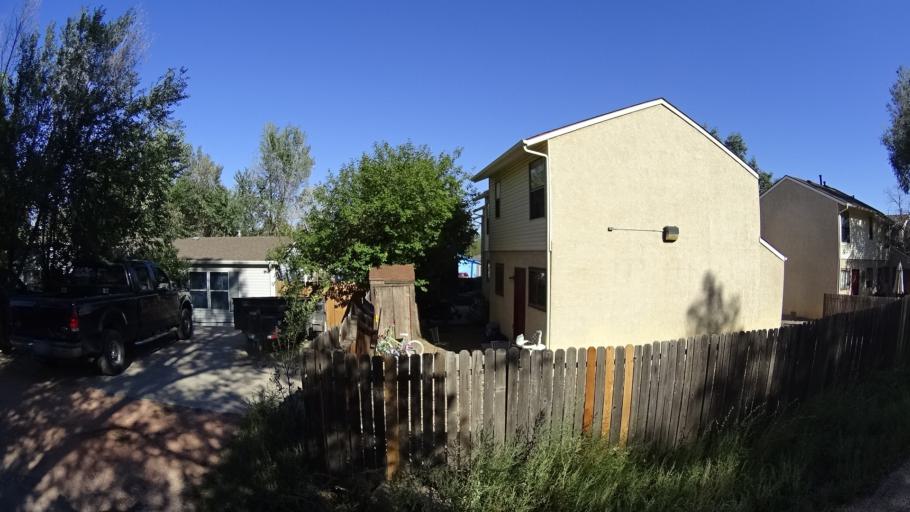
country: US
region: Colorado
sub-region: El Paso County
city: Colorado Springs
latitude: 38.8380
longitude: -104.8682
